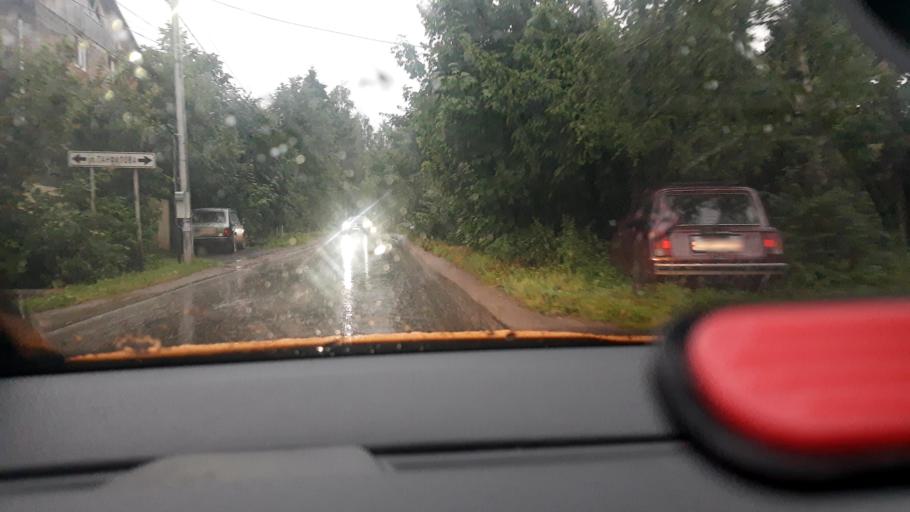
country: RU
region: Moskovskaya
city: Alabushevo
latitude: 56.0046
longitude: 37.1309
